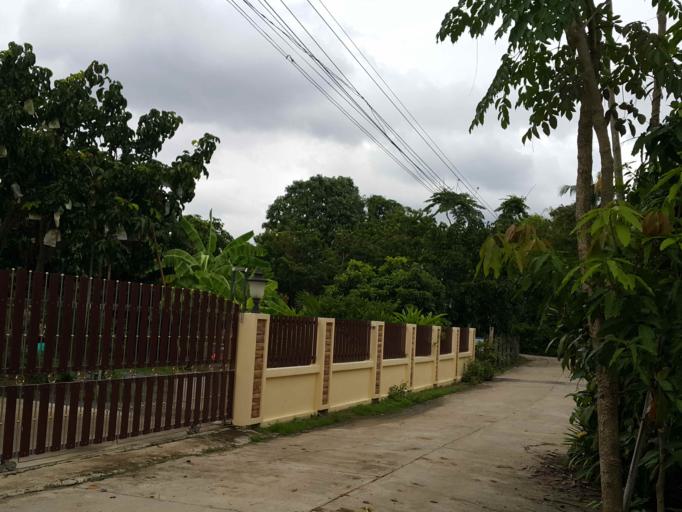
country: TH
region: Chiang Mai
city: San Sai
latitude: 18.8254
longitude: 99.0687
